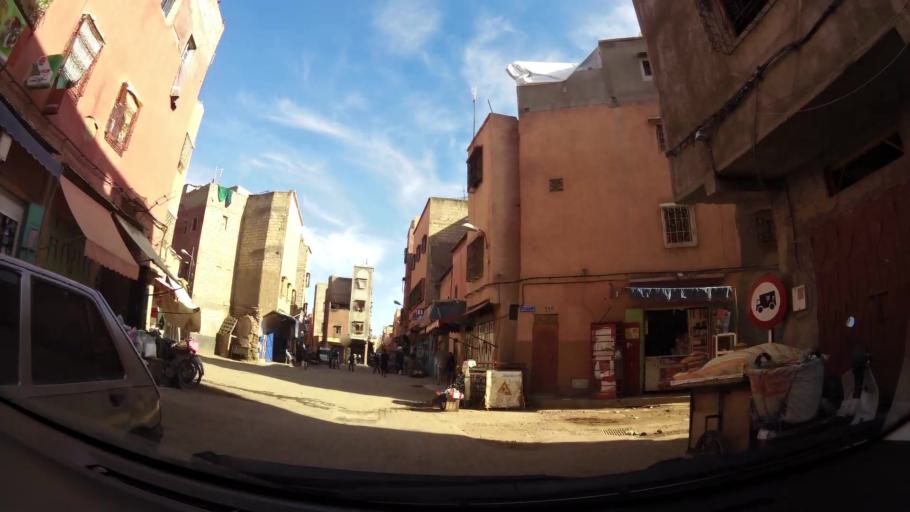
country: MA
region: Marrakech-Tensift-Al Haouz
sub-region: Marrakech
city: Marrakesh
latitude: 31.6124
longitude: -7.9606
